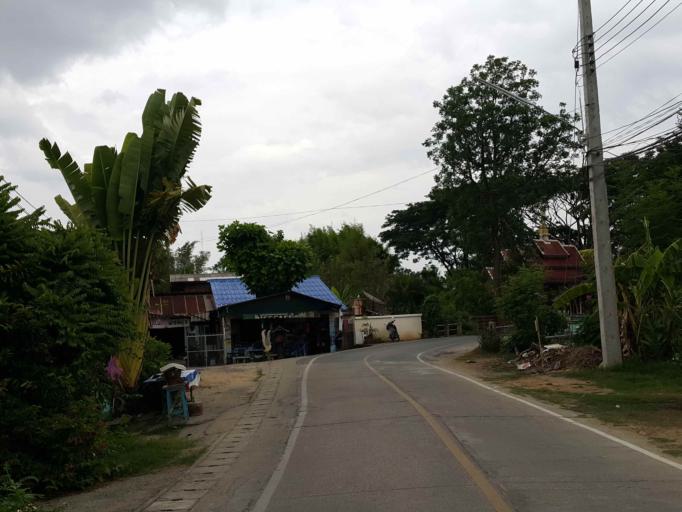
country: TH
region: Chiang Mai
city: Chiang Mai
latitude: 18.7512
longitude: 99.0011
